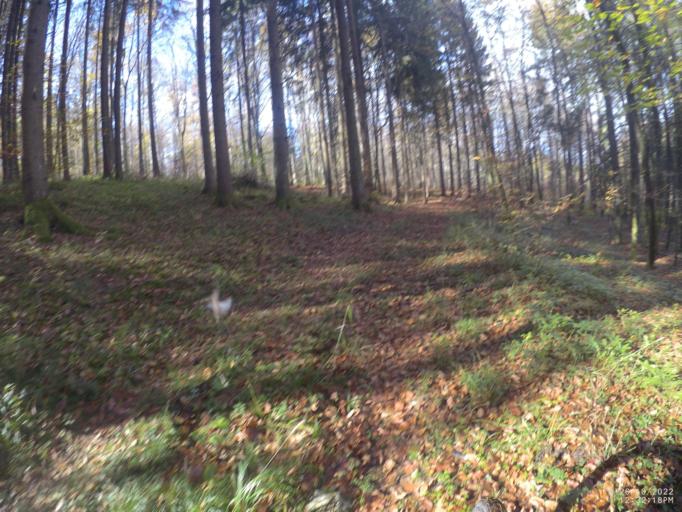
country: DE
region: Baden-Wuerttemberg
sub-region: Regierungsbezirk Stuttgart
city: Wiesensteig
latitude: 48.5442
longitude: 9.6066
